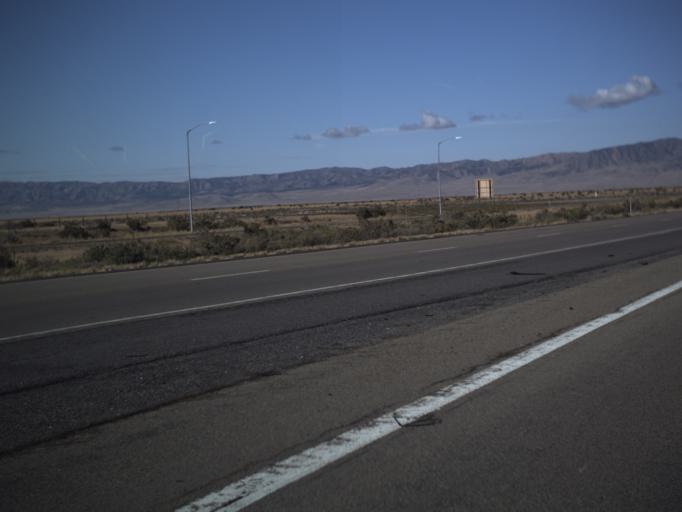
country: US
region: Utah
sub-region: Tooele County
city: Grantsville
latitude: 40.7466
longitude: -112.6568
